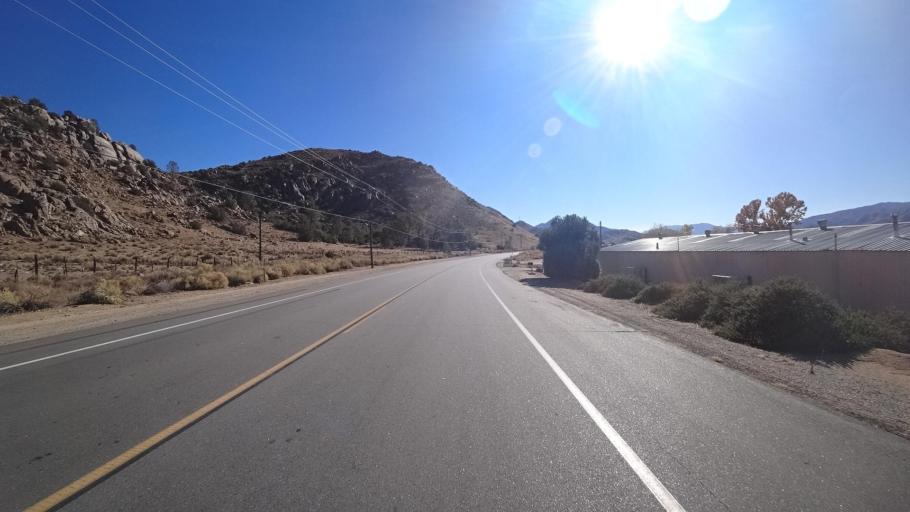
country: US
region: California
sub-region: Kern County
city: Kernville
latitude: 35.7220
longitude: -118.4169
